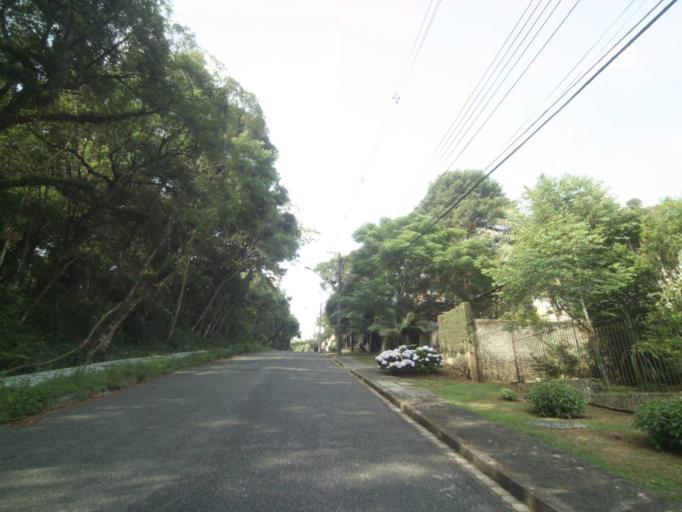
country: BR
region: Parana
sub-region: Curitiba
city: Curitiba
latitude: -25.4120
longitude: -49.3156
